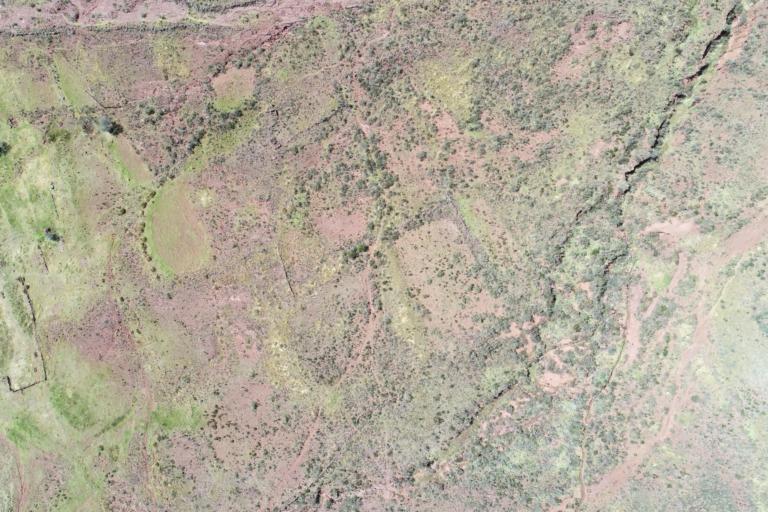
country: BO
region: La Paz
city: Tiahuanaco
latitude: -16.6066
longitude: -68.7677
